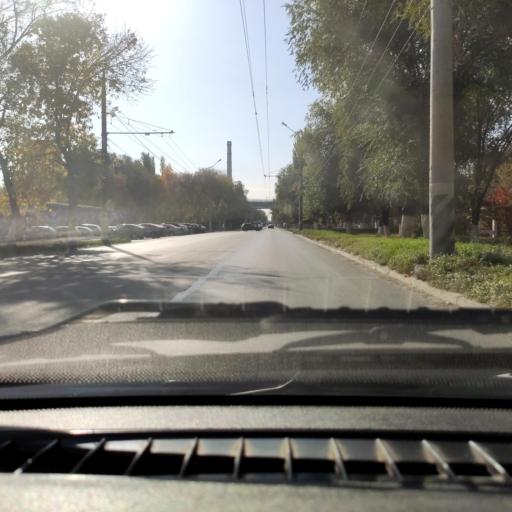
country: RU
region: Samara
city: Tol'yatti
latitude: 53.5581
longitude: 49.4527
